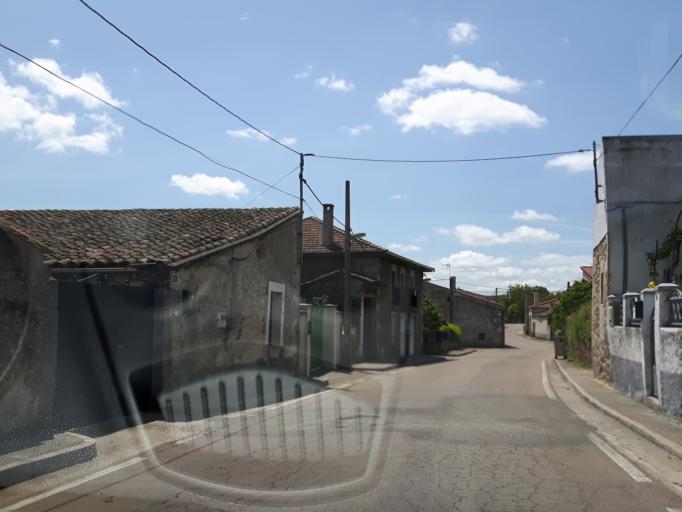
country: ES
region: Castille and Leon
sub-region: Provincia de Salamanca
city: Aldea del Obispo
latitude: 40.7076
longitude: -6.7949
